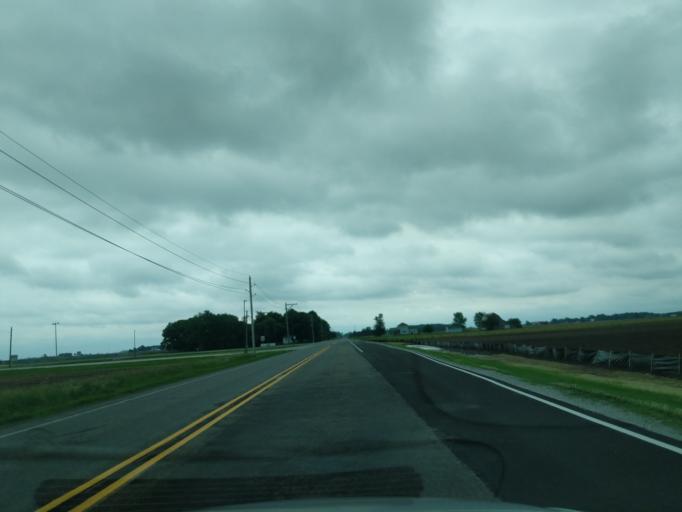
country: US
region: Indiana
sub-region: Tipton County
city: Tipton
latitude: 40.2834
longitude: -86.0057
